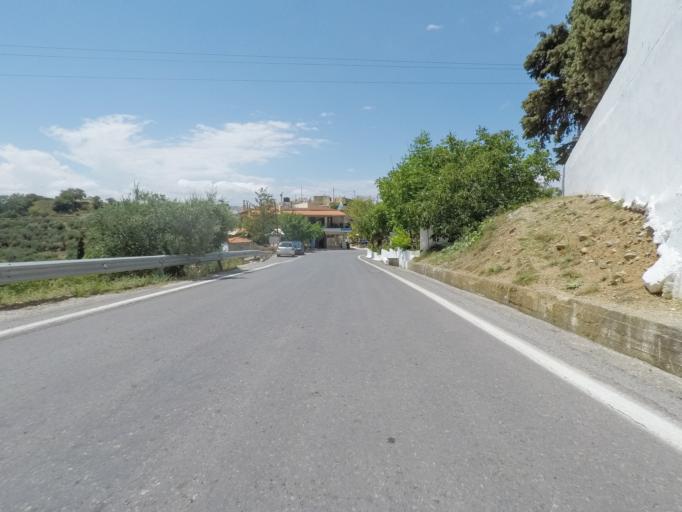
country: GR
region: Crete
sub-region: Nomos Irakleiou
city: Mokhos
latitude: 35.2195
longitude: 25.4606
